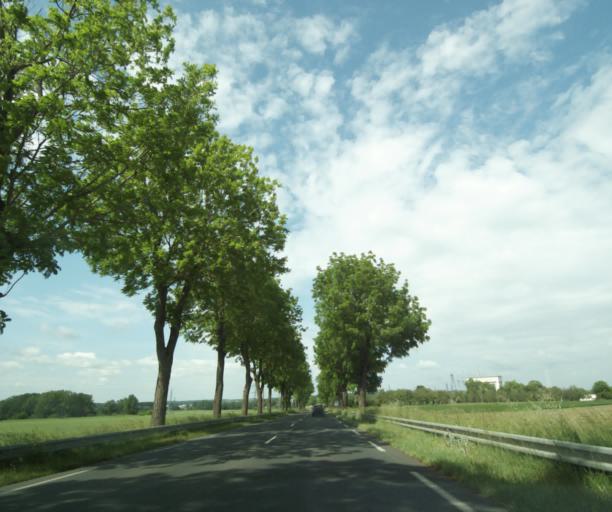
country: FR
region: Pays de la Loire
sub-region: Departement de Maine-et-Loire
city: Distre
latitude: 47.2060
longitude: -0.1200
